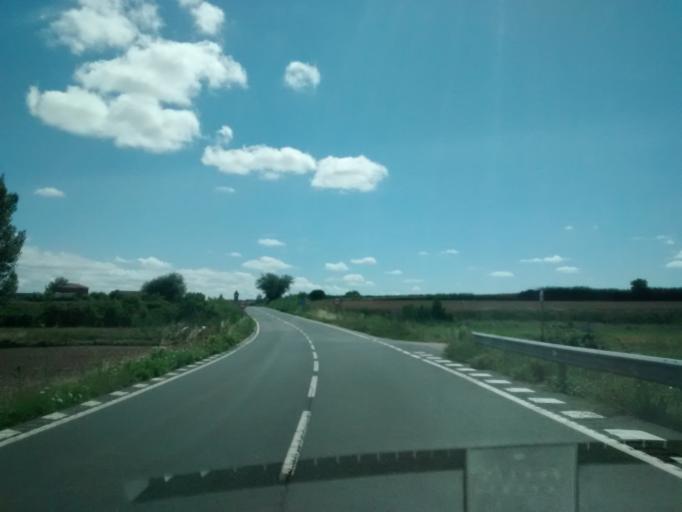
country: ES
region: La Rioja
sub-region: Provincia de La Rioja
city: Villamediana de Iregua
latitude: 42.4166
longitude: -2.3797
